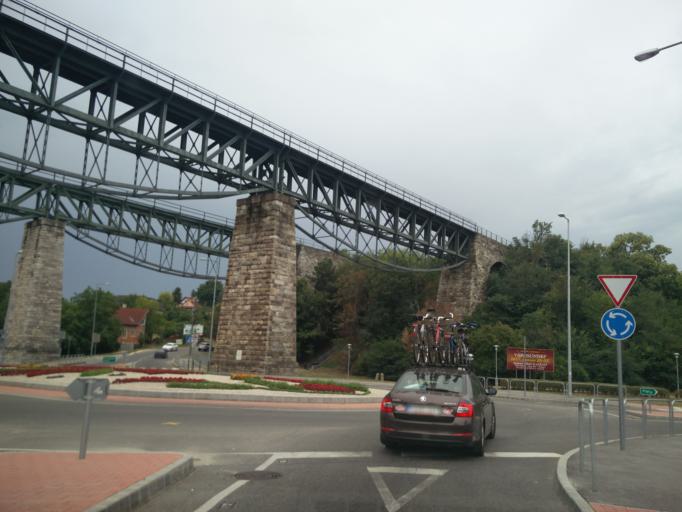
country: HU
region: Pest
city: Biatorbagy
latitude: 47.4723
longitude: 18.8330
